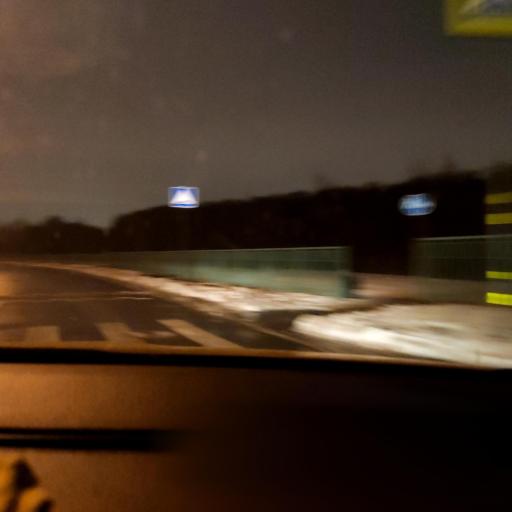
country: RU
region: Moscow
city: Nekrasovka
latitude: 55.7189
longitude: 37.8860
